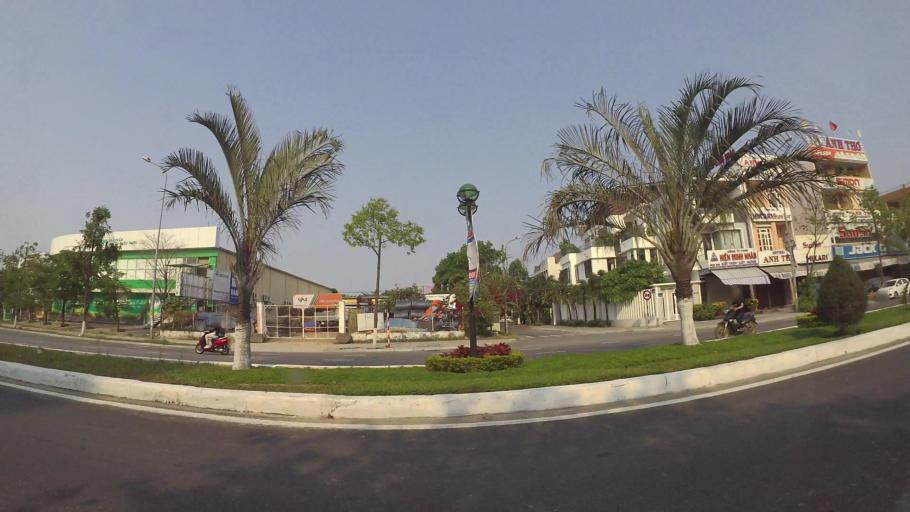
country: VN
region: Da Nang
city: Cam Le
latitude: 16.0236
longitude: 108.2094
